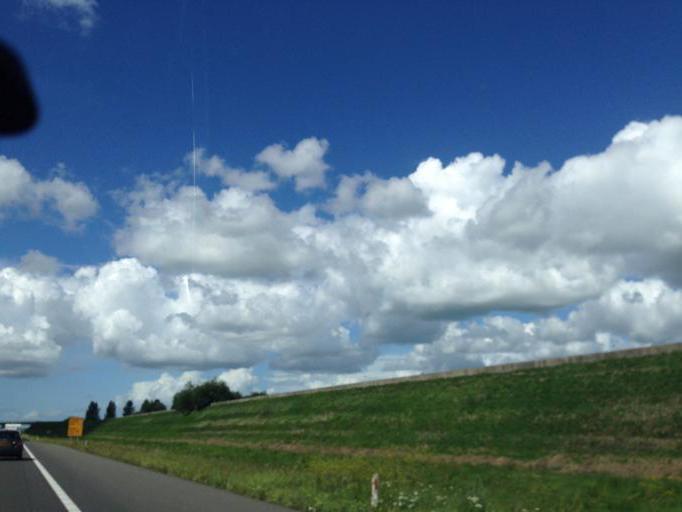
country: NL
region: Overijssel
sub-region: Gemeente Kampen
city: Kampen
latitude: 52.5394
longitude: 5.9021
